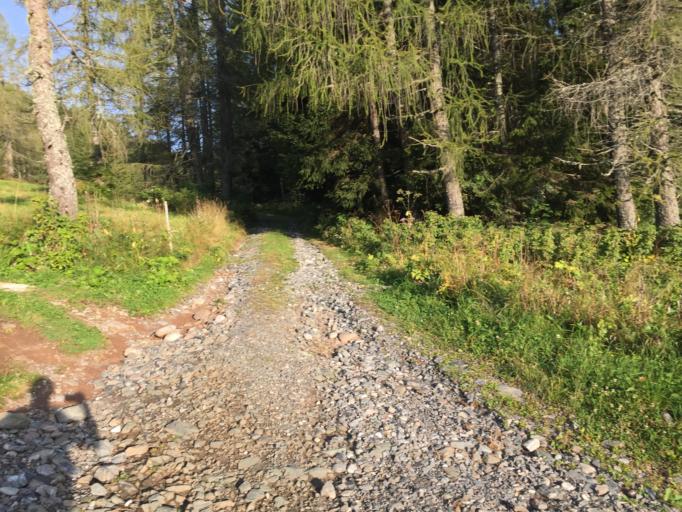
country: IT
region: Friuli Venezia Giulia
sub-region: Provincia di Udine
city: Prato Carnico
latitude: 46.5547
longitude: 12.8095
